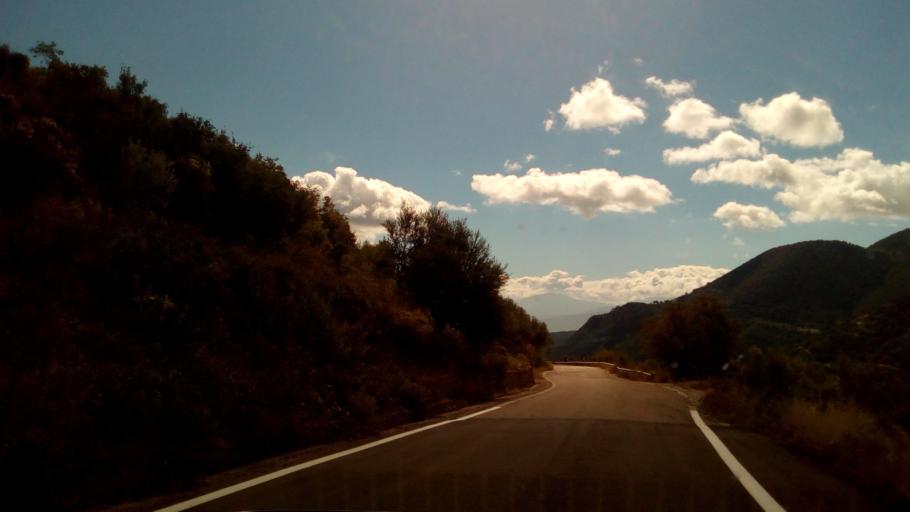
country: GR
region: West Greece
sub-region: Nomos Aitolias kai Akarnanias
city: Nafpaktos
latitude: 38.4813
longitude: 21.8634
